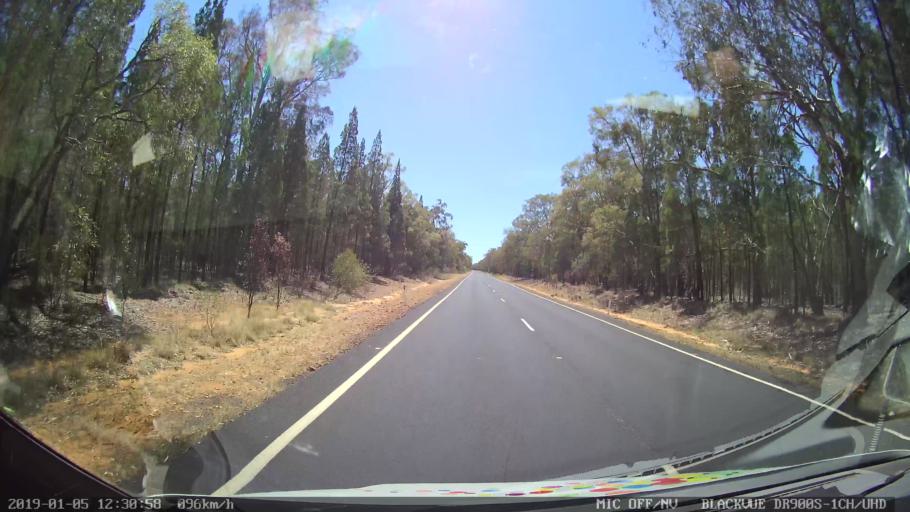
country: AU
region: New South Wales
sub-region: Warrumbungle Shire
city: Coonabarabran
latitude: -31.2244
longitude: 149.3581
